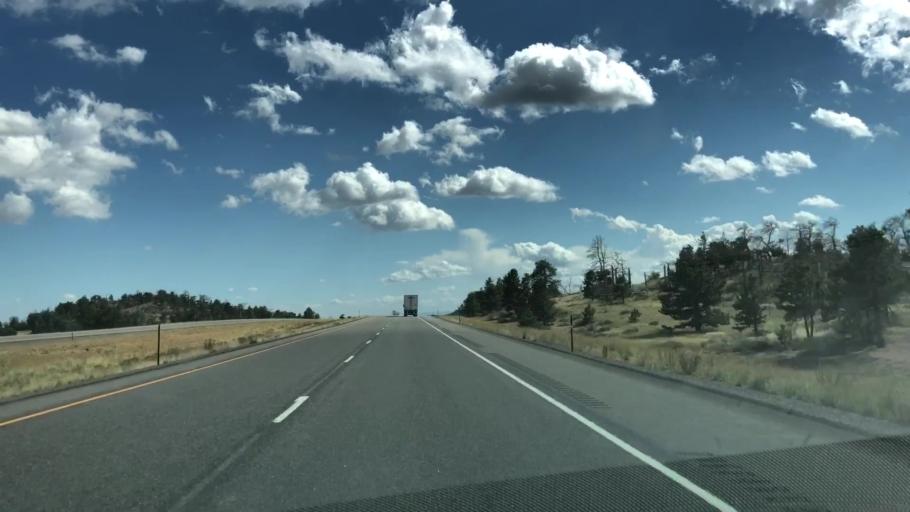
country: US
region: Wyoming
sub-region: Albany County
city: Laramie
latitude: 41.0157
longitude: -105.4205
